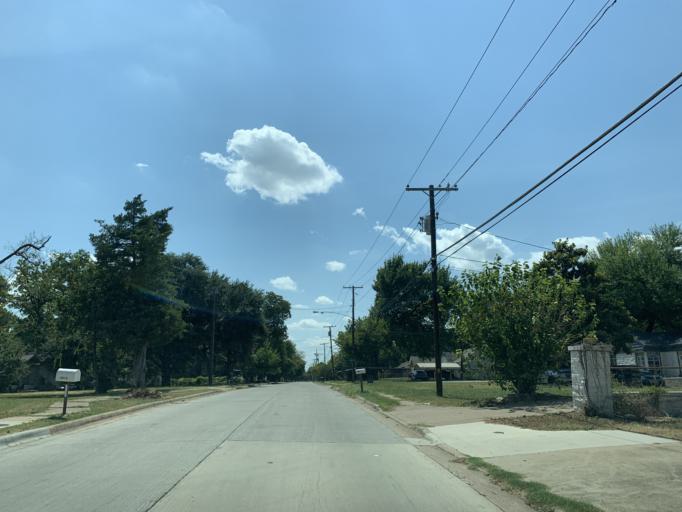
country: US
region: Texas
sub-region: Dallas County
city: Hutchins
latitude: 32.7096
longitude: -96.7681
